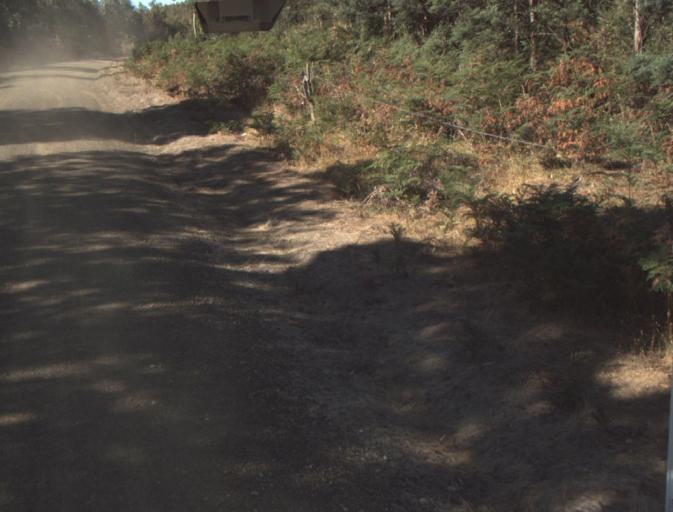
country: AU
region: Tasmania
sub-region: Dorset
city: Scottsdale
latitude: -41.2695
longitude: 147.3763
